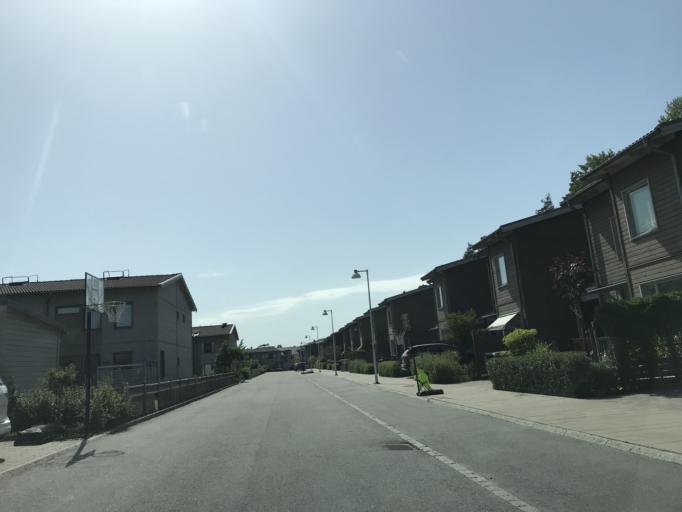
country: SE
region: Stockholm
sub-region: Solna Kommun
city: Rasunda
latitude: 59.3863
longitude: 17.9817
